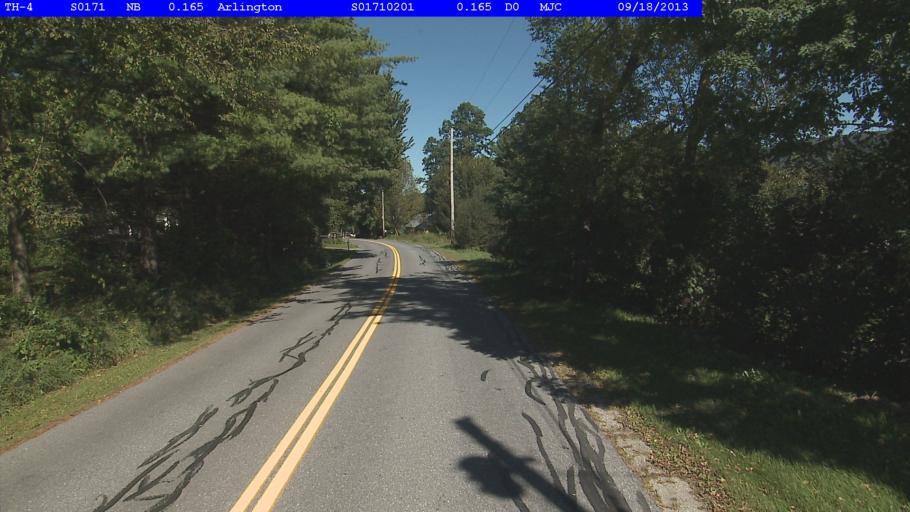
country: US
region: Vermont
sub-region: Bennington County
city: Arlington
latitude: 43.0559
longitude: -73.1499
